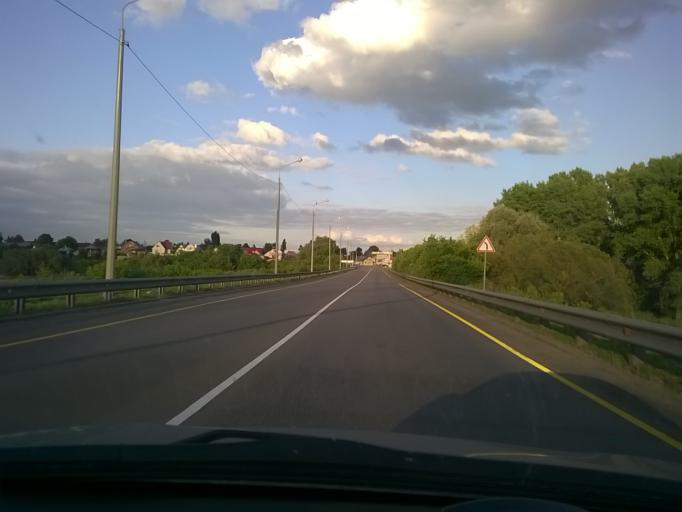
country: RU
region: Voronezj
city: Borisoglebsk
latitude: 51.3755
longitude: 42.0552
